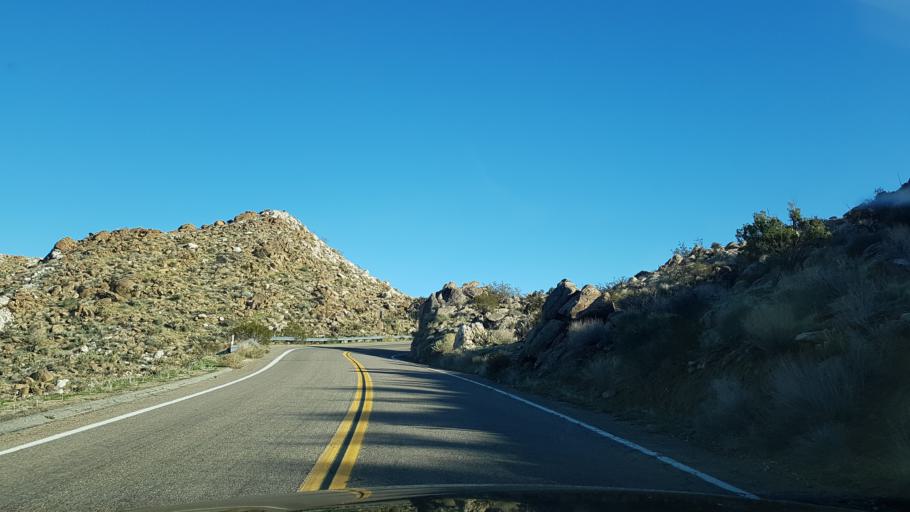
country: US
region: California
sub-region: San Diego County
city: Julian
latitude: 33.0399
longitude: -116.4110
